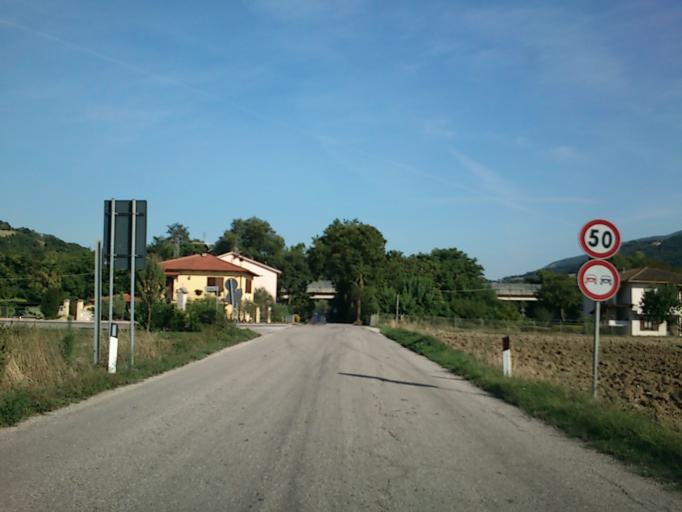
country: IT
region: The Marches
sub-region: Provincia di Pesaro e Urbino
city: Canavaccio
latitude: 43.6886
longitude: 12.7138
